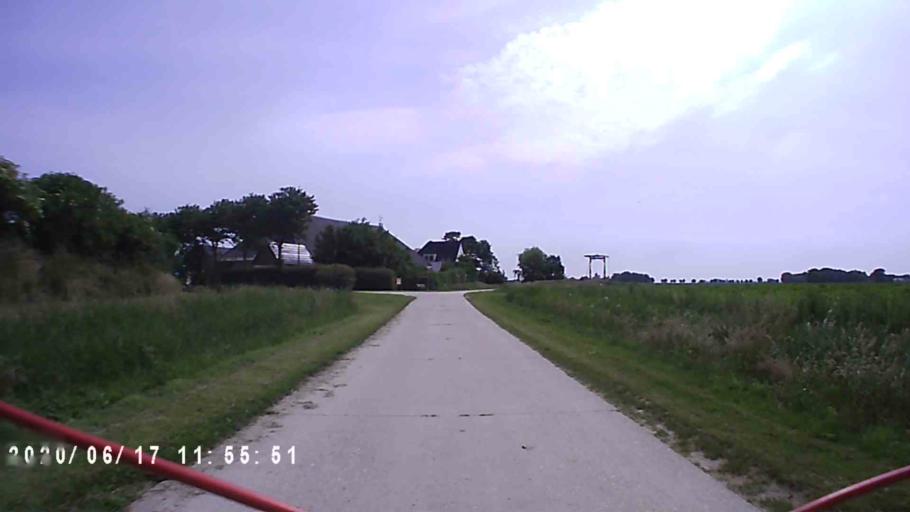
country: NL
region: Groningen
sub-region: Gemeente De Marne
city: Ulrum
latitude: 53.3490
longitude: 6.3185
